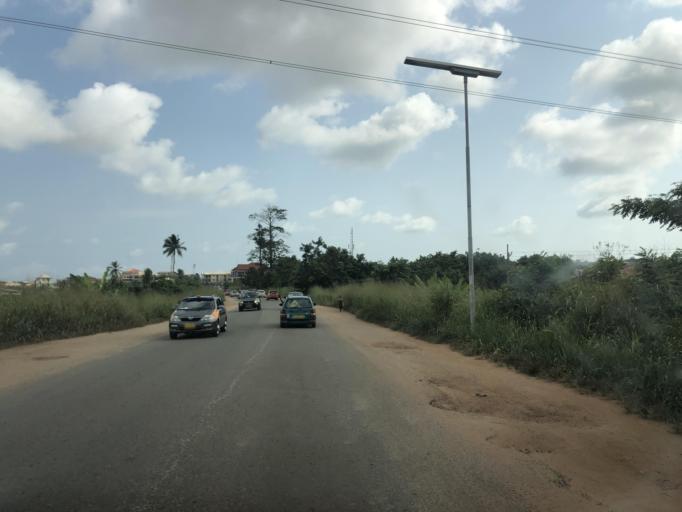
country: GH
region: Central
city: Cape Coast
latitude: 5.1471
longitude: -1.2875
